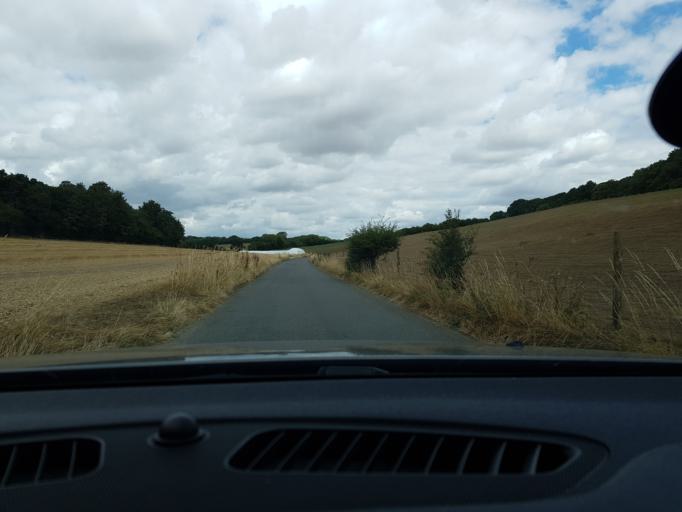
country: GB
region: England
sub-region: West Berkshire
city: Kintbury
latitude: 51.4298
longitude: -1.4755
